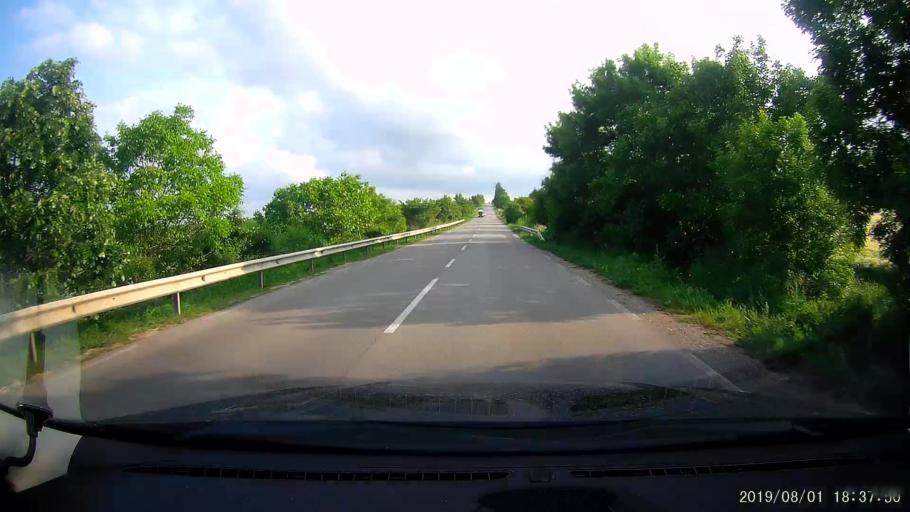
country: BG
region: Shumen
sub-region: Obshtina Khitrino
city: Gara Khitrino
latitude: 43.4131
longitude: 26.9248
